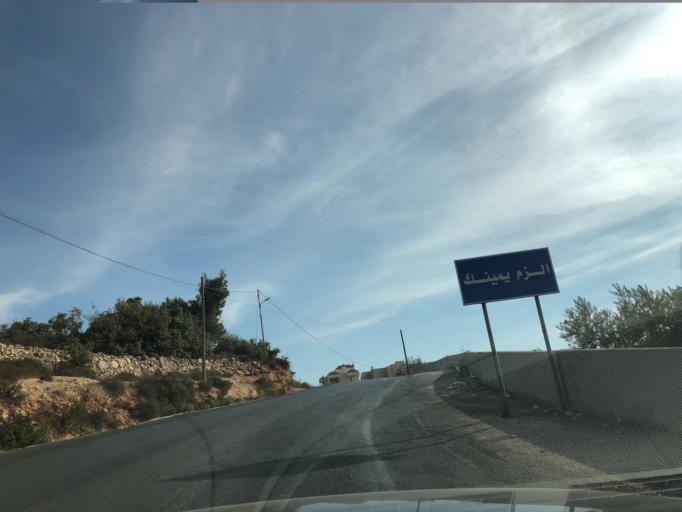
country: JO
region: Irbid
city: `Ayn Jannah
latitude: 32.3273
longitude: 35.7606
